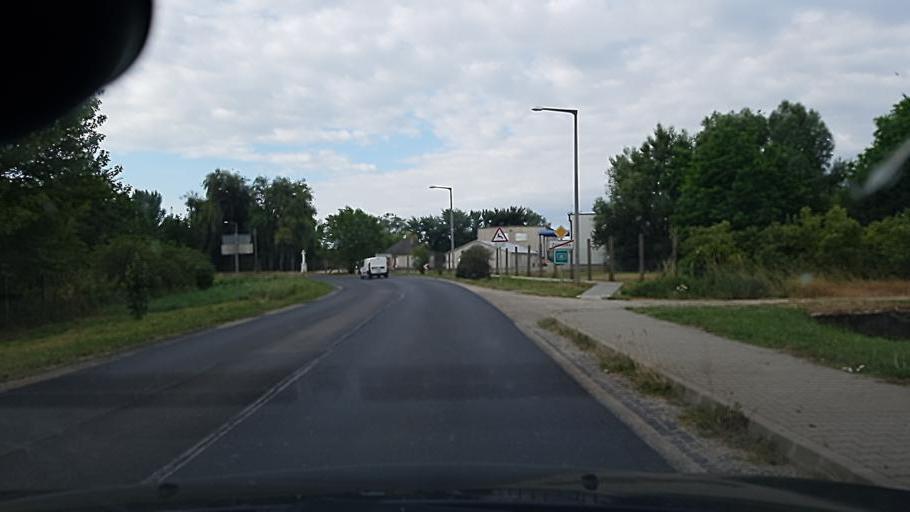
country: HU
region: Pest
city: Zsambek
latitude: 47.5389
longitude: 18.7231
